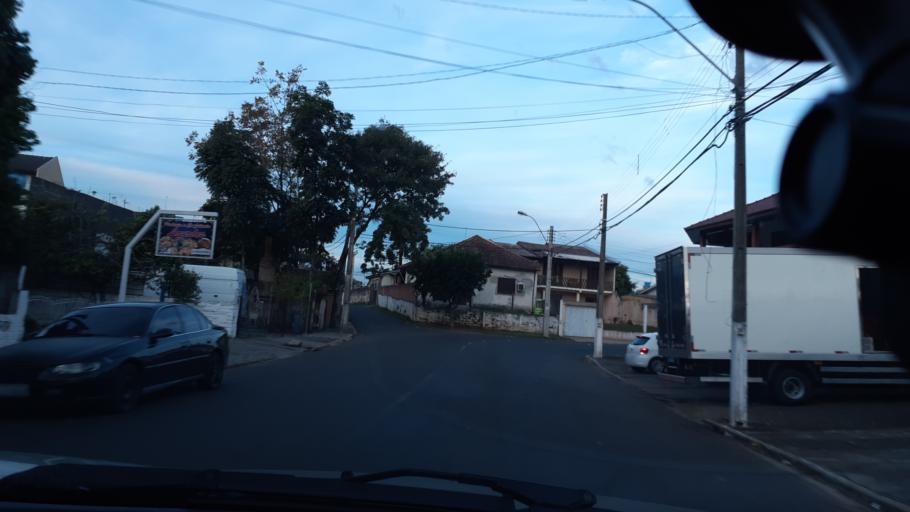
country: BR
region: Rio Grande do Sul
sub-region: Sapucaia Do Sul
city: Sapucaia
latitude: -29.8431
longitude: -51.1503
